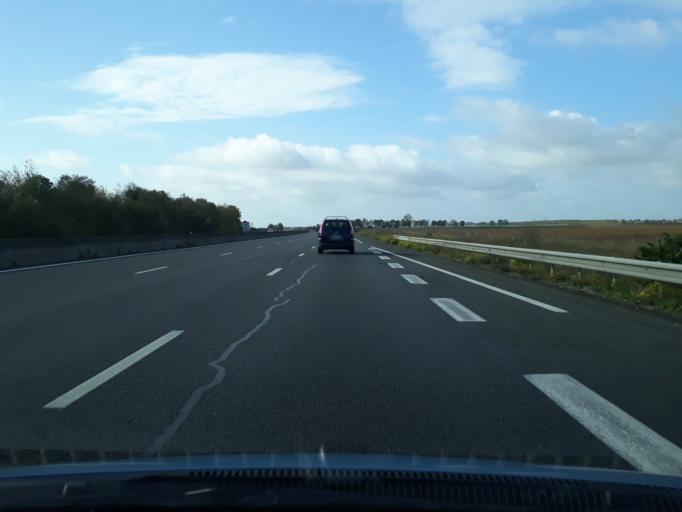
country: FR
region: Centre
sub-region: Departement du Loiret
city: Beaugency
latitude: 47.8170
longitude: 1.6353
